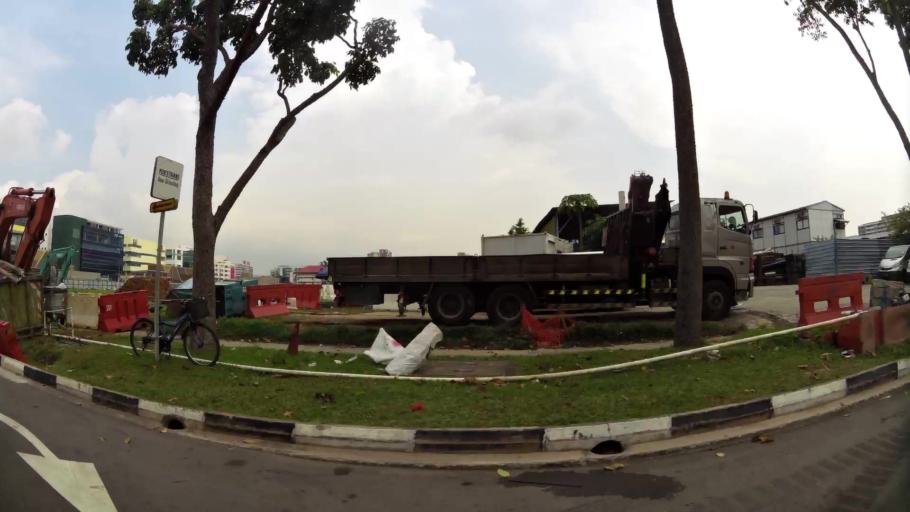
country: SG
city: Singapore
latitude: 1.3287
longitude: 103.8985
